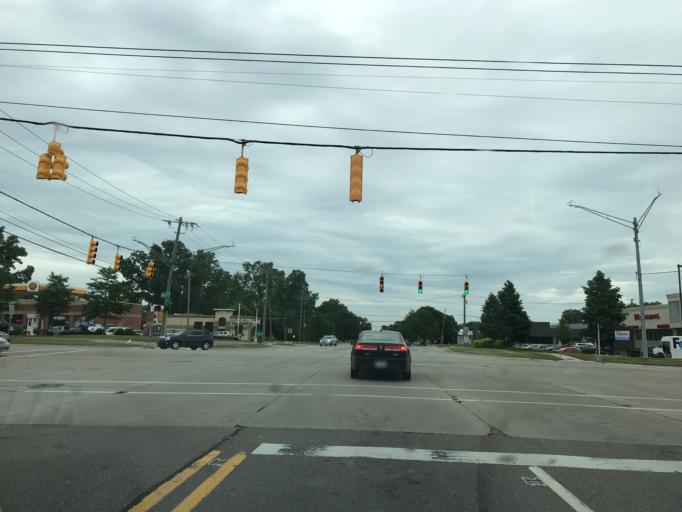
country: US
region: Michigan
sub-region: Oakland County
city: Farmington
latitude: 42.4701
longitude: -83.3577
